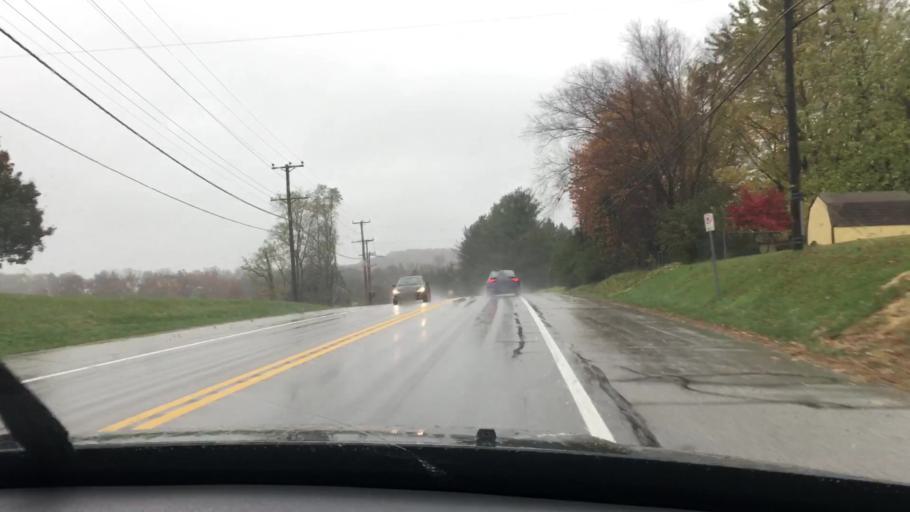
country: US
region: Maryland
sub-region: Carroll County
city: Manchester
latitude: 39.6734
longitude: -76.8918
